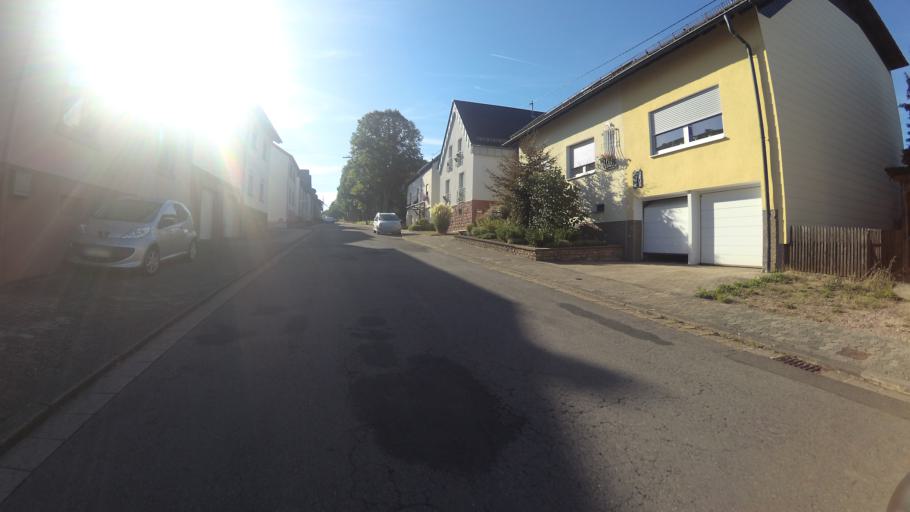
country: DE
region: Saarland
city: Eppelborn
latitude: 49.4455
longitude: 6.9598
